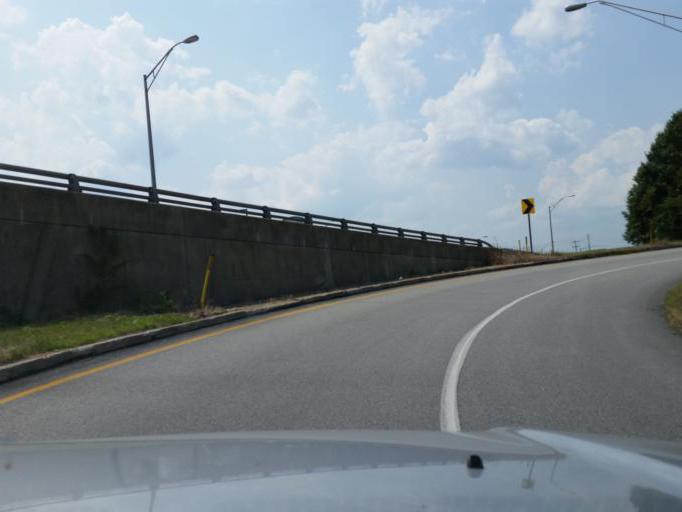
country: US
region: Pennsylvania
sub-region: Dauphin County
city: Lawnton
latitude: 40.2523
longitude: -76.8146
